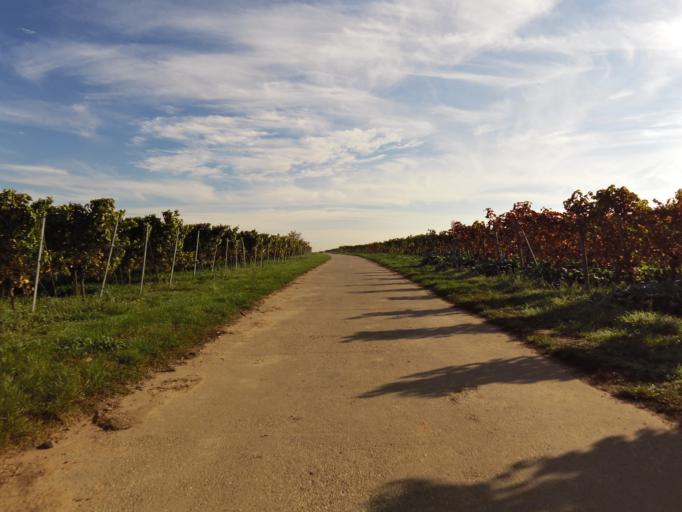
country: DE
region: Rheinland-Pfalz
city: Friedelsheim
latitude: 49.4600
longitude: 8.1997
